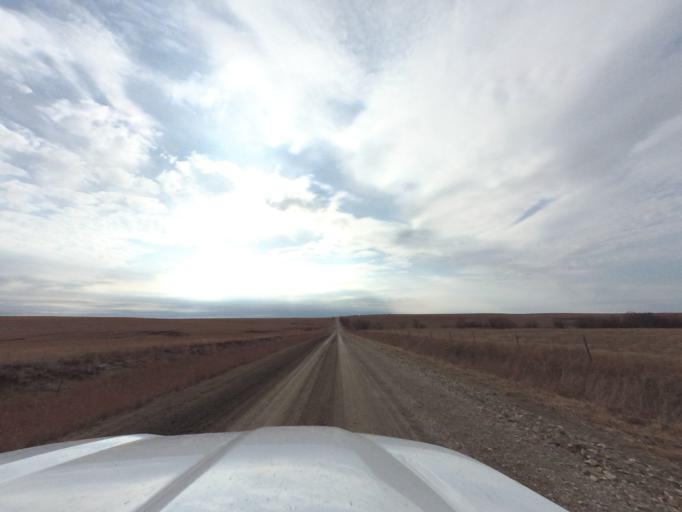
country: US
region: Kansas
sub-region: Chase County
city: Cottonwood Falls
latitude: 38.2292
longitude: -96.7307
